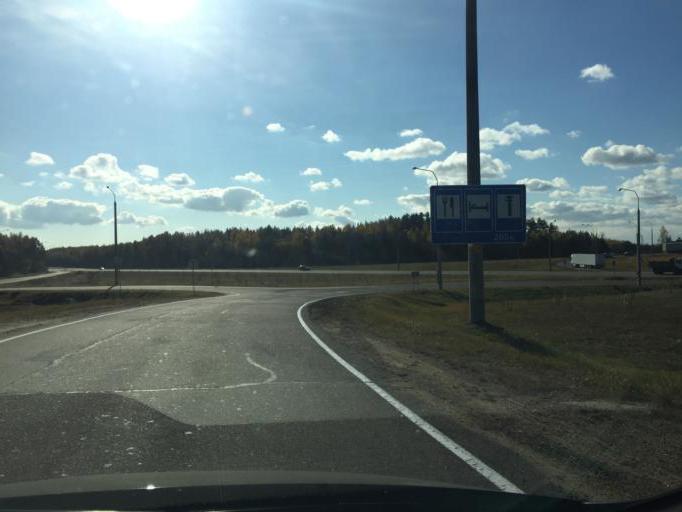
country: BY
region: Minsk
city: Slabada
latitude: 53.9489
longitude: 27.9798
